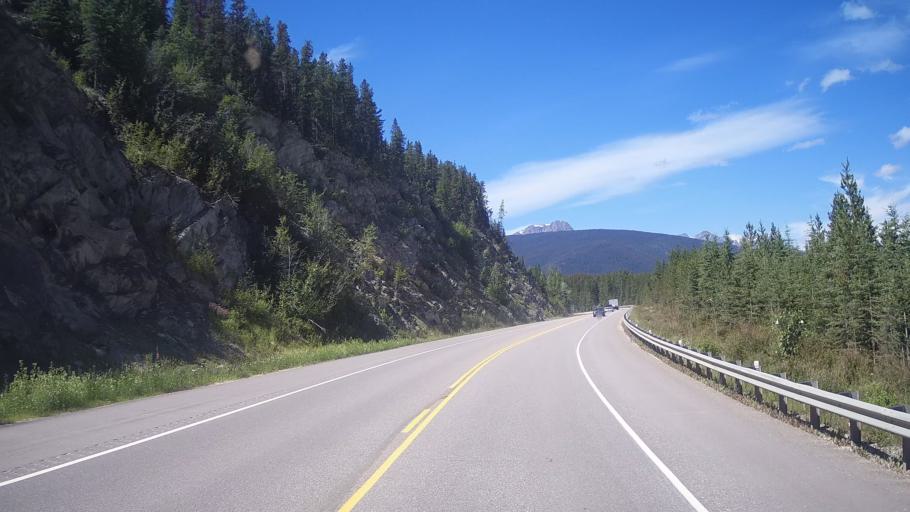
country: CA
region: Alberta
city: Jasper Park Lodge
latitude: 52.8822
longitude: -118.4355
